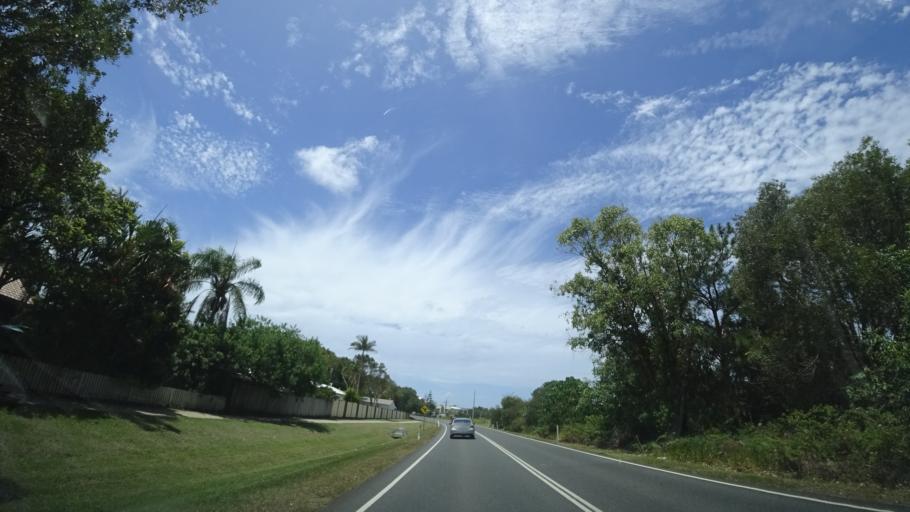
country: AU
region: Queensland
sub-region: Sunshine Coast
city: Mooloolaba
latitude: -26.6080
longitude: 153.0959
